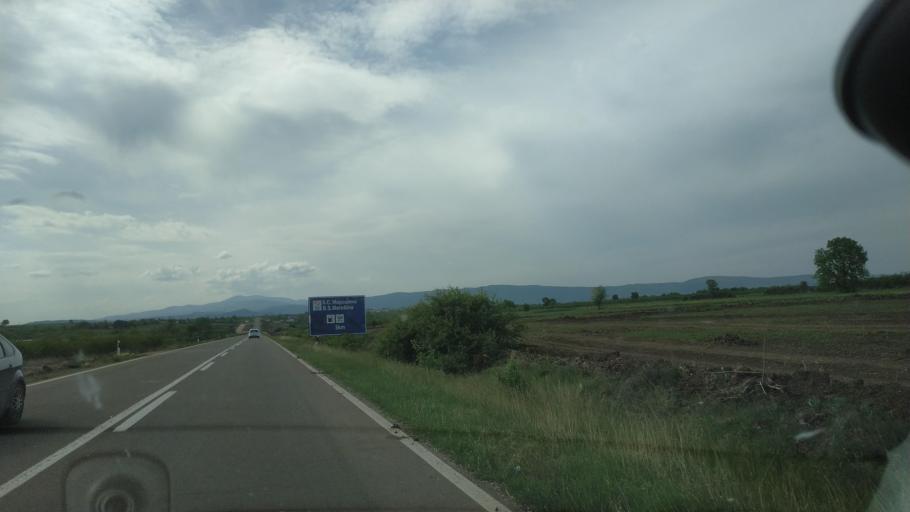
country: RS
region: Central Serbia
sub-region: Nisavski Okrug
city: Merosina
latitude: 43.2814
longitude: 21.7765
